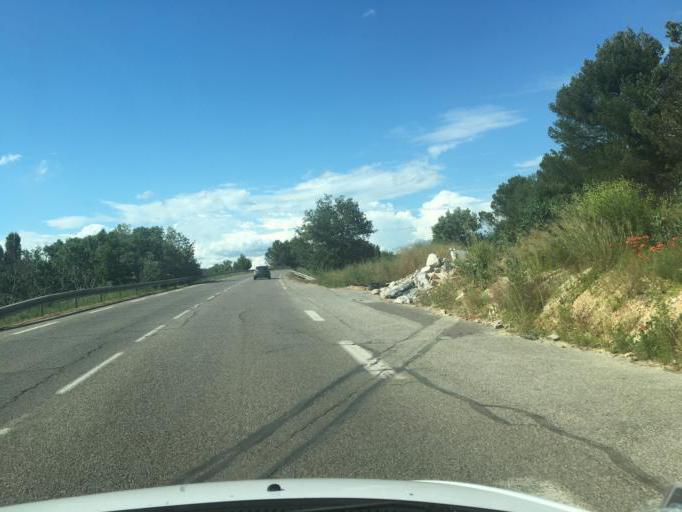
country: FR
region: Provence-Alpes-Cote d'Azur
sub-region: Departement des Bouches-du-Rhone
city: Eguilles
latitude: 43.5345
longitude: 5.3488
